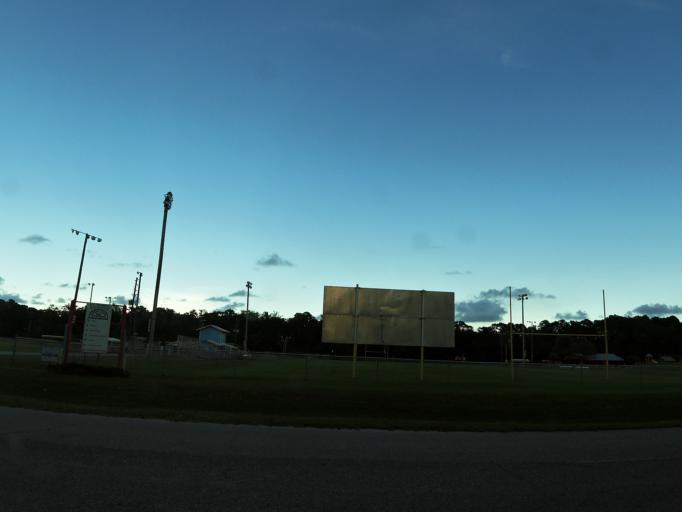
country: US
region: Georgia
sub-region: Camden County
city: St. Marys
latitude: 30.7348
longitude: -81.5542
